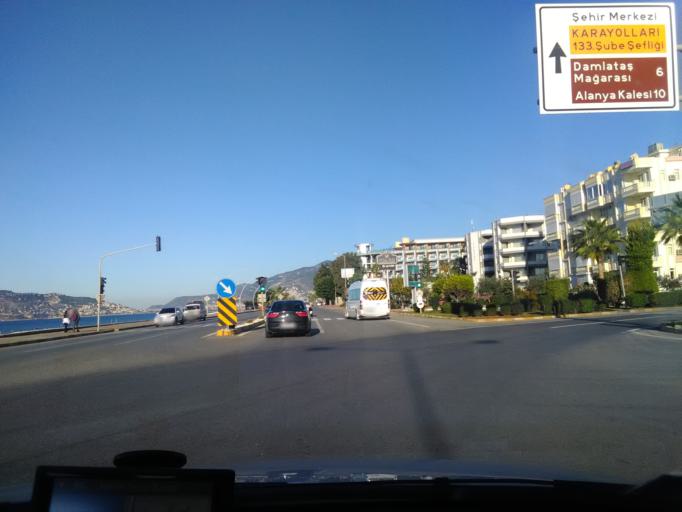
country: TR
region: Antalya
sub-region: Alanya
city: Mahmutlar
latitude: 36.5260
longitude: 32.0494
